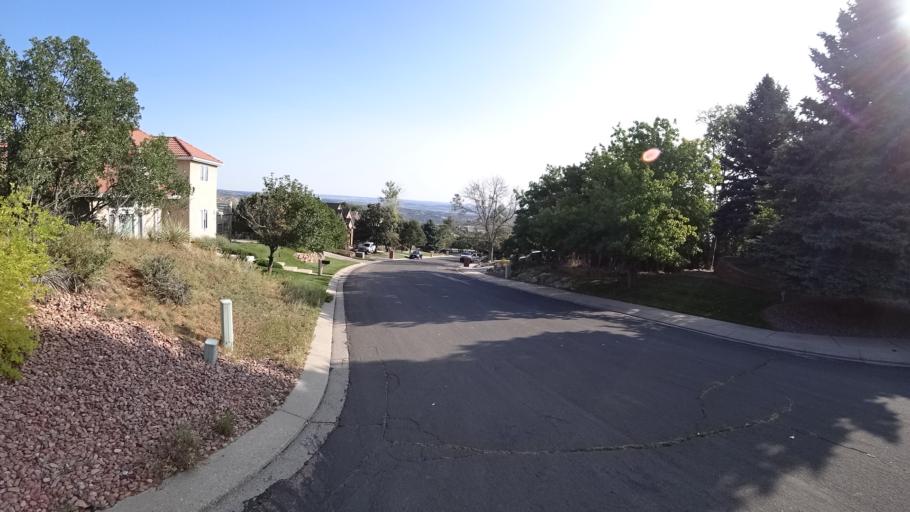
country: US
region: Colorado
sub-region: El Paso County
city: Manitou Springs
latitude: 38.8212
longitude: -104.8818
